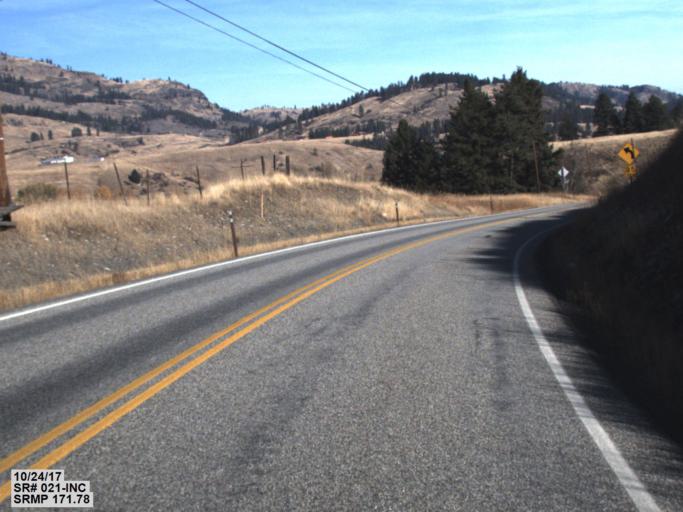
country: US
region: Washington
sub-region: Ferry County
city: Republic
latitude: 48.7671
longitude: -118.6469
